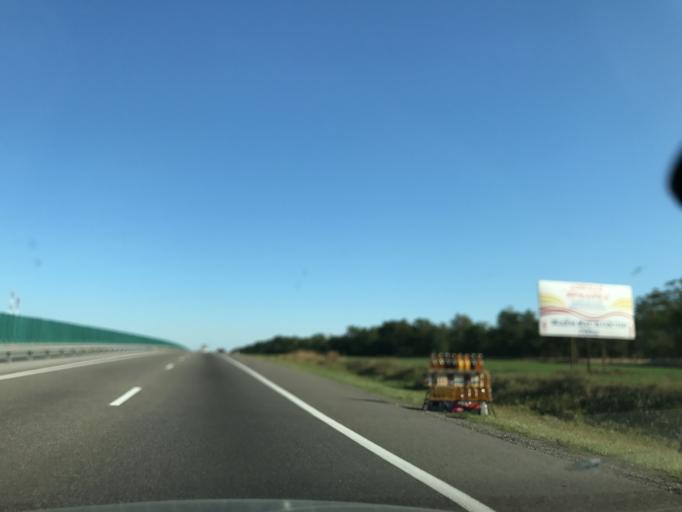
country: RU
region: Rostov
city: Glubokiy
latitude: 48.6212
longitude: 40.3556
